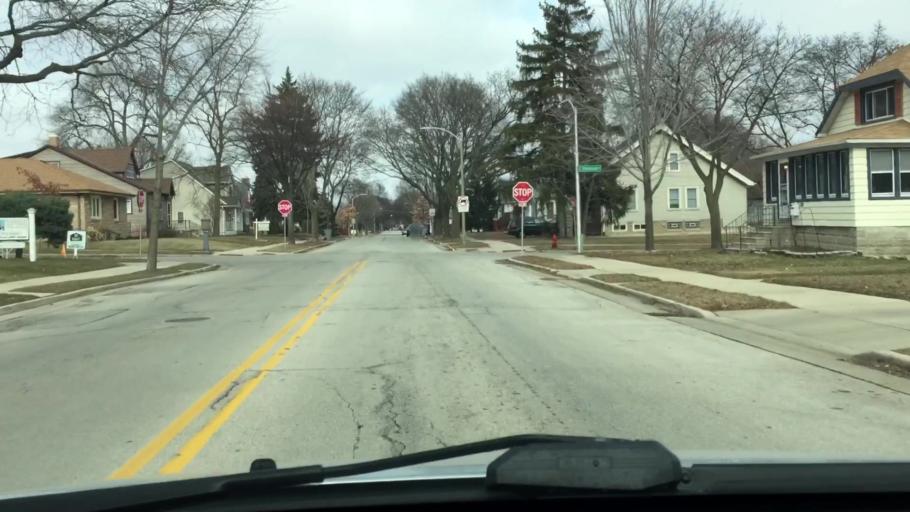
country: US
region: Wisconsin
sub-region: Milwaukee County
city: West Allis
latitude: 43.0318
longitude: -87.9998
